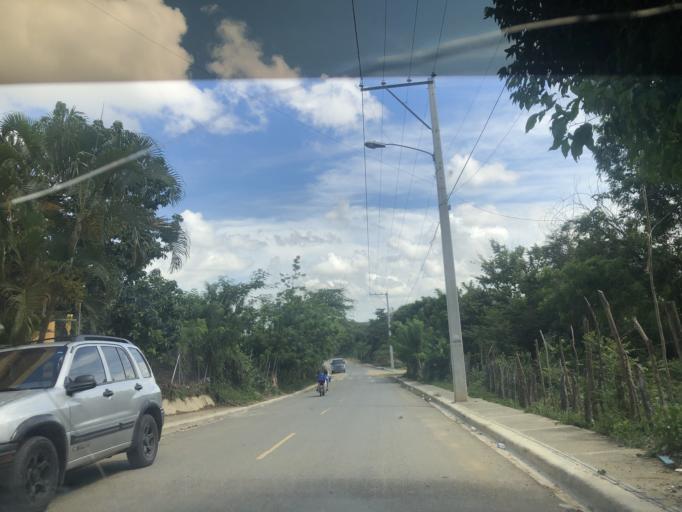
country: DO
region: Santiago
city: Santiago de los Caballeros
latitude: 19.4081
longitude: -70.7030
